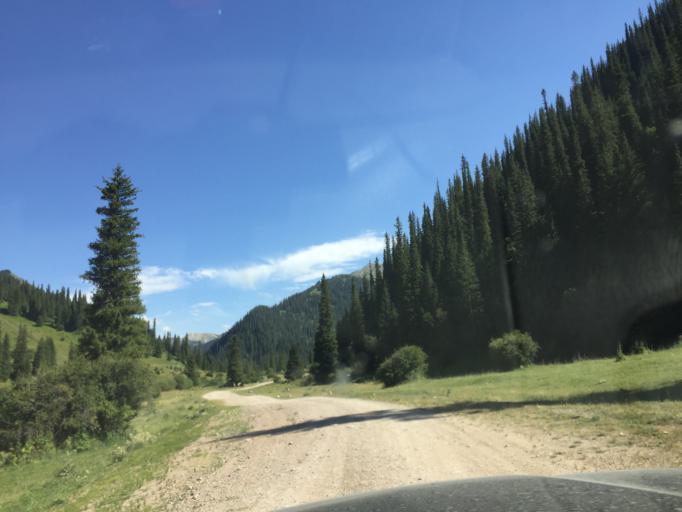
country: KZ
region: Almaty Oblysy
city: Kegen
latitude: 42.6639
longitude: 79.2091
